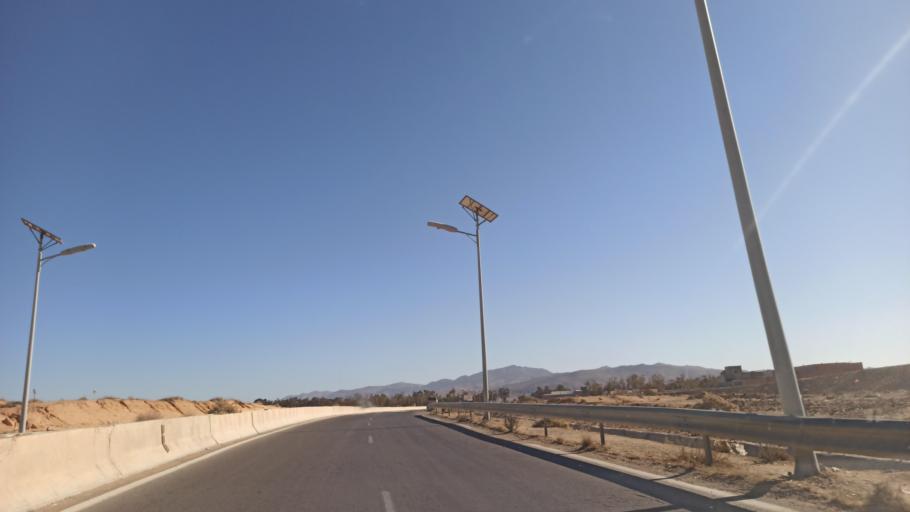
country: TN
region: Gafsa
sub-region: Gafsa Municipality
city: Gafsa
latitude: 34.4328
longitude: 8.8115
